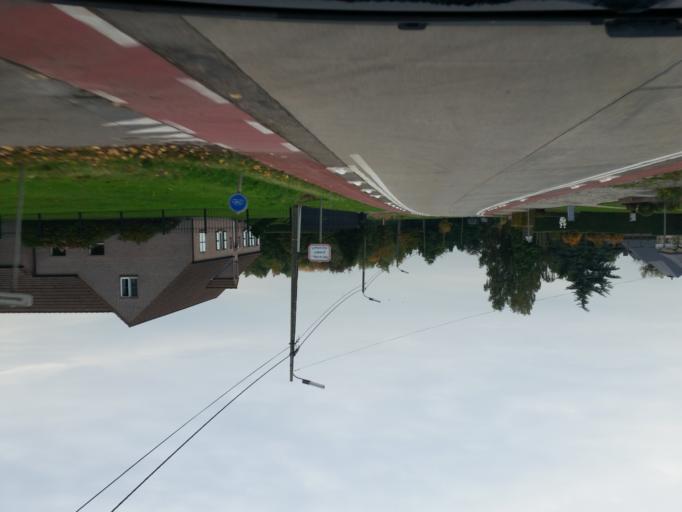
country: BE
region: Flanders
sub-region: Provincie Antwerpen
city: Sint-Katelijne-Waver
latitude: 51.0596
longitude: 4.5514
